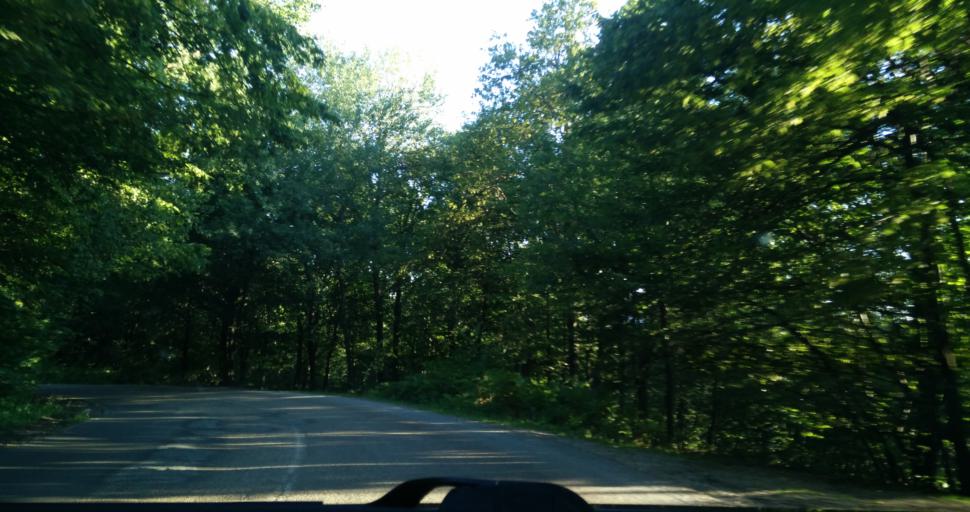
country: RO
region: Bihor
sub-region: Oras Nucet
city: Nucet
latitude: 46.4917
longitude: 22.6072
